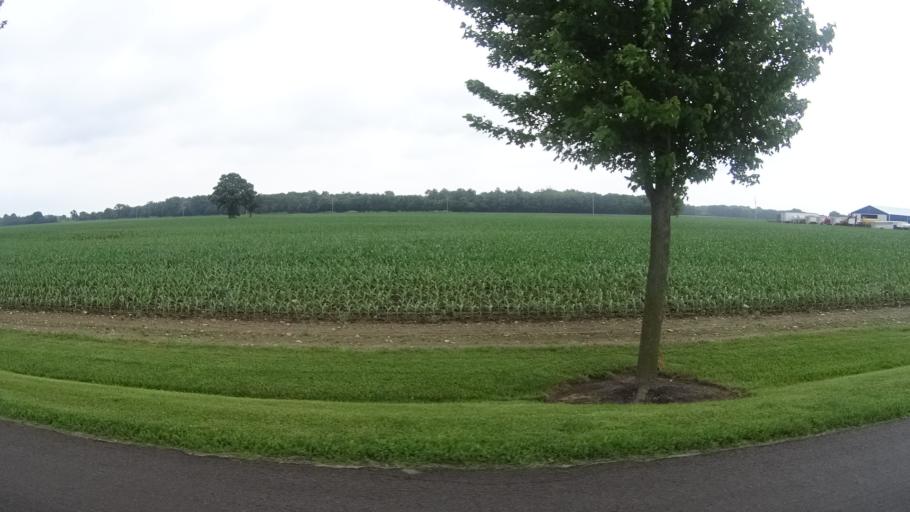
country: US
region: Ohio
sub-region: Huron County
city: Bellevue
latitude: 41.3536
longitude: -82.7856
